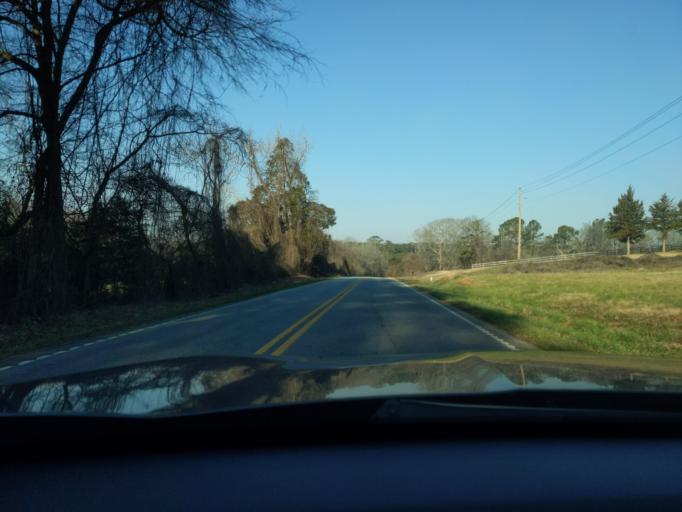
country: US
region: South Carolina
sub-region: Greenwood County
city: Ninety Six
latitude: 34.1741
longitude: -82.0884
